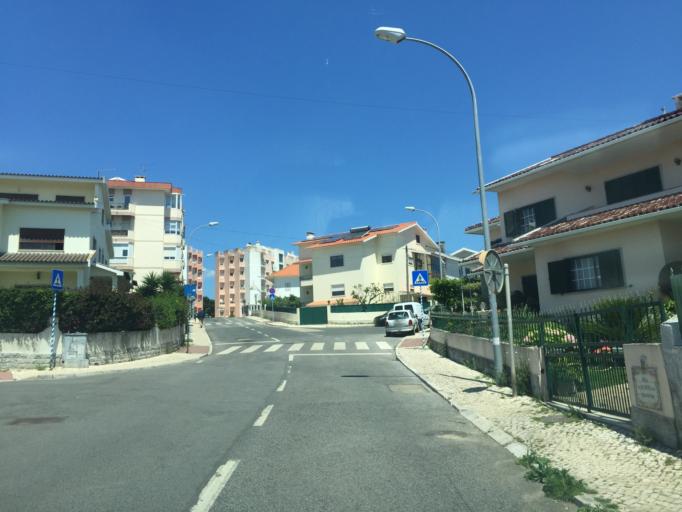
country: PT
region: Lisbon
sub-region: Oeiras
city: Quejas
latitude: 38.7212
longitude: -9.2661
